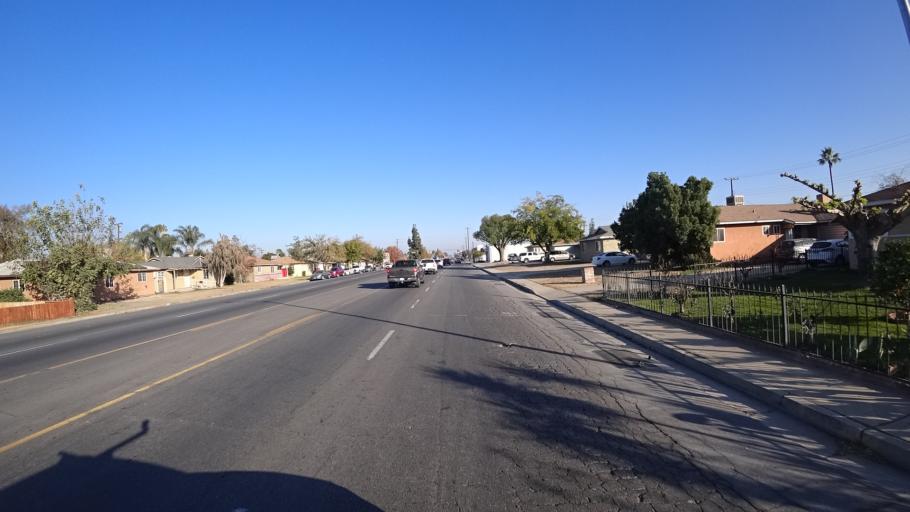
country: US
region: California
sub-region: Kern County
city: Bakersfield
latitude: 35.3394
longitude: -119.0233
